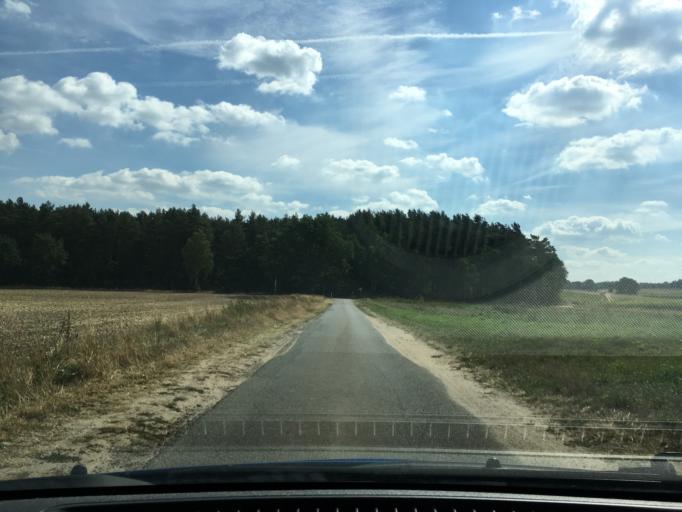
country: DE
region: Lower Saxony
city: Gohrde
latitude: 53.1211
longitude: 10.9507
